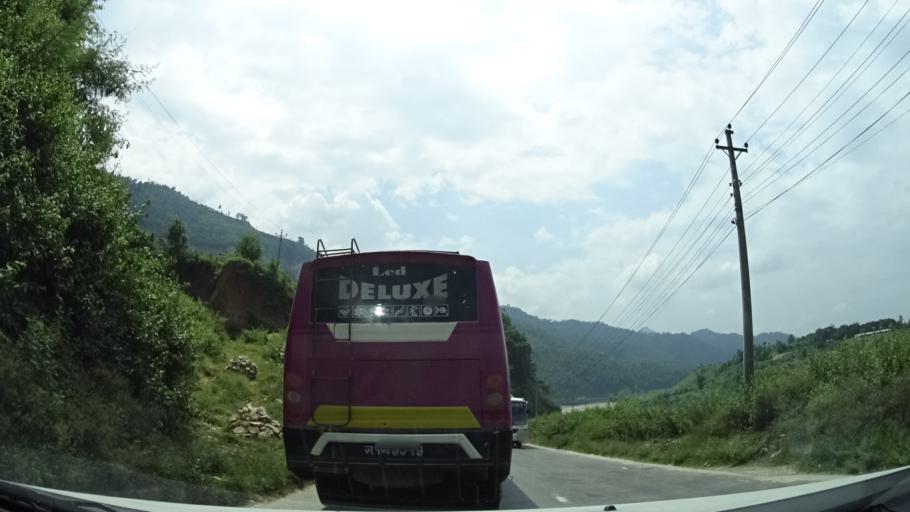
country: NP
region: Central Region
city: Kirtipur
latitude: 27.8014
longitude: 84.9327
